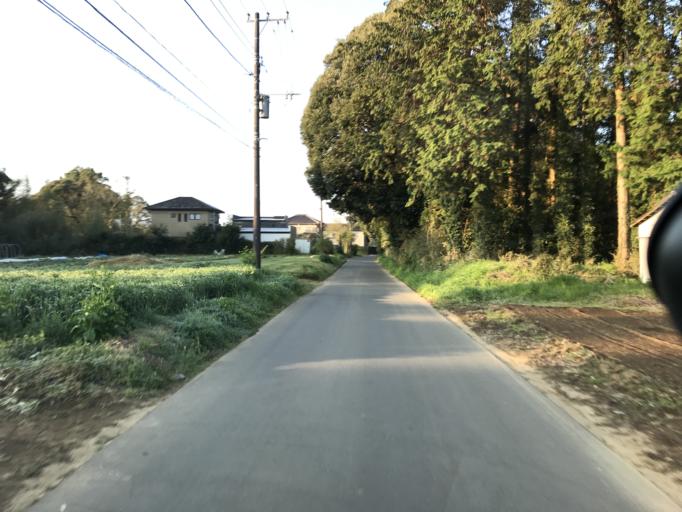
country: JP
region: Chiba
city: Yokaichiba
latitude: 35.7883
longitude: 140.5445
